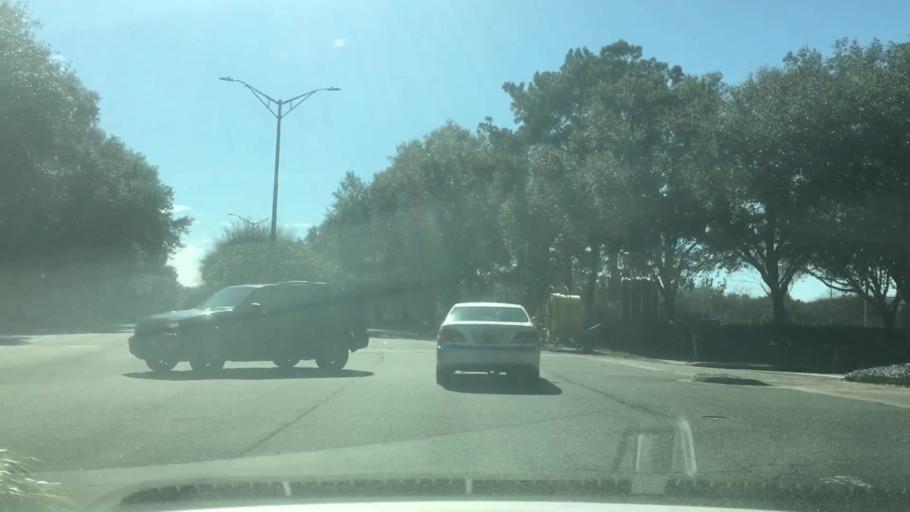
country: US
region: Florida
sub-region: Duval County
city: Jacksonville
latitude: 30.2465
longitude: -81.5432
